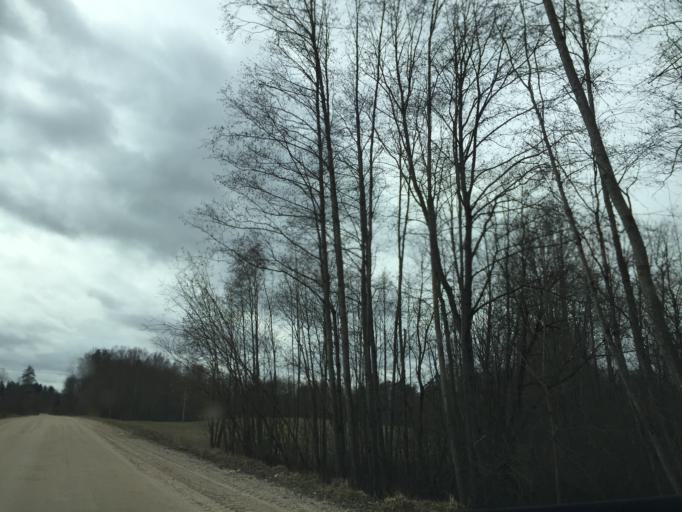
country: LV
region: Kraslavas Rajons
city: Kraslava
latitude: 55.9692
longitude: 27.0712
